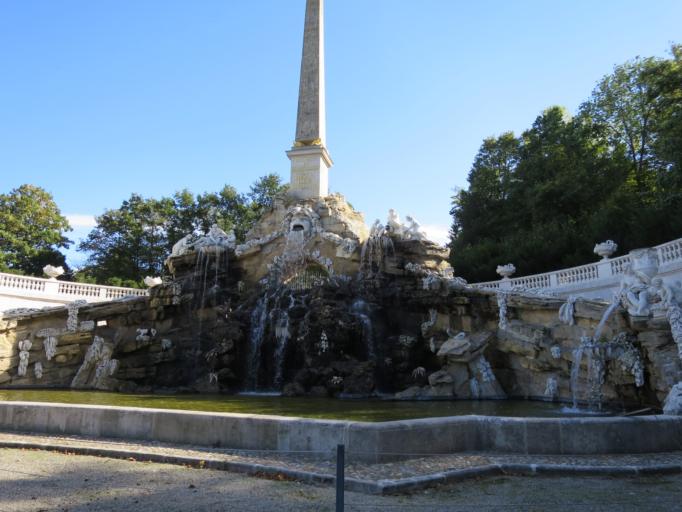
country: AT
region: Vienna
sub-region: Wien Stadt
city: Vienna
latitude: 48.1802
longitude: 16.3158
